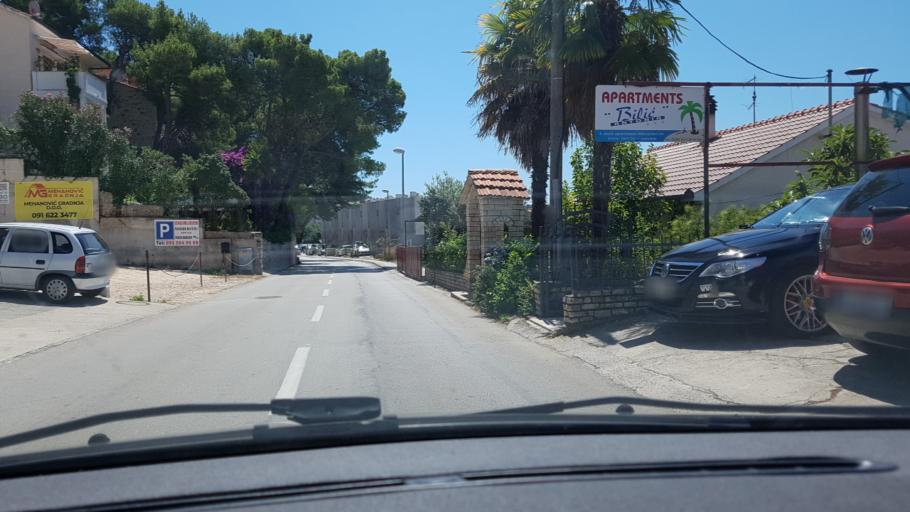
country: HR
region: Splitsko-Dalmatinska
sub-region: Grad Trogir
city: Trogir
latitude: 43.5093
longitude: 16.2561
